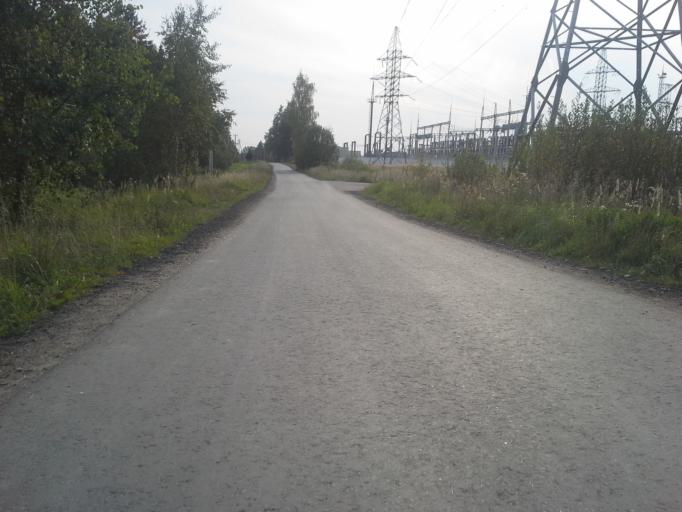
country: RU
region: Moskovskaya
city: Aprelevka
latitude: 55.5657
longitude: 37.0721
